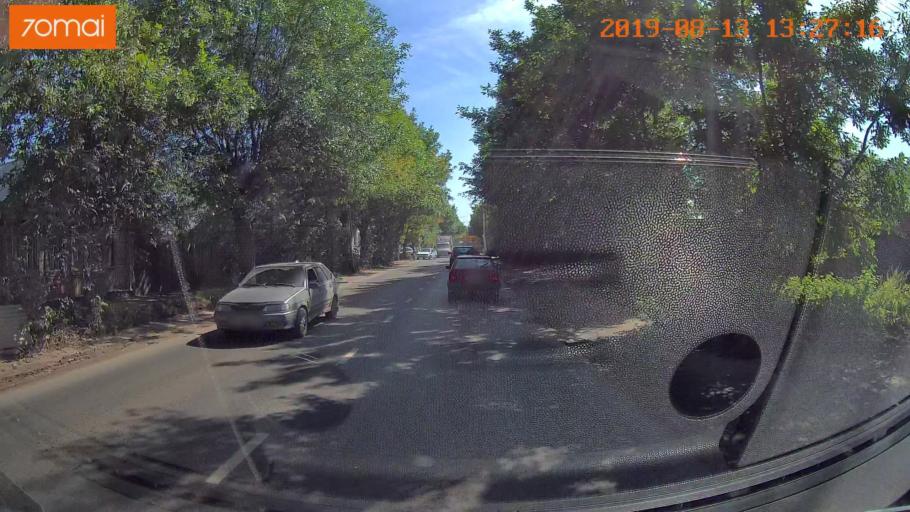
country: RU
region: Ivanovo
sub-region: Gorod Ivanovo
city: Ivanovo
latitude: 56.9957
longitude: 40.9513
